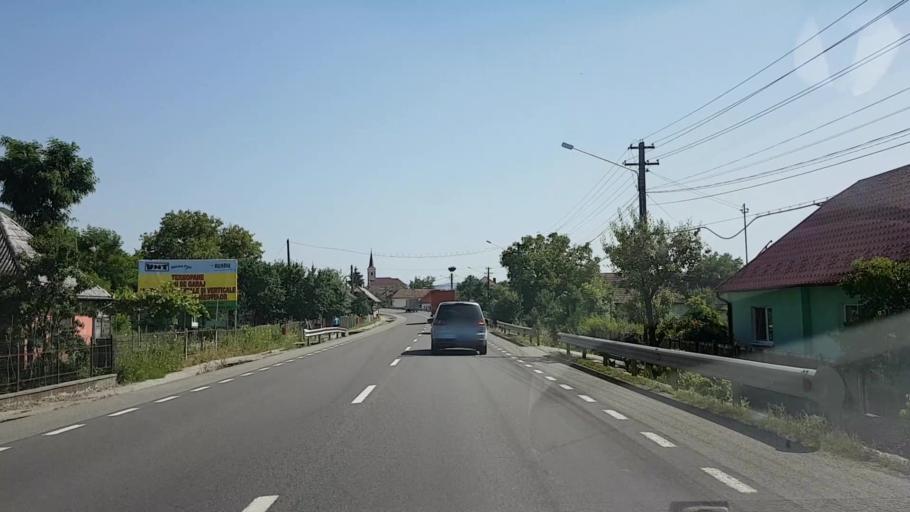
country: RO
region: Bistrita-Nasaud
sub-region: Comuna Sieu-Odorhei
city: Sieu-Odorhei
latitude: 47.1501
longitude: 24.3058
